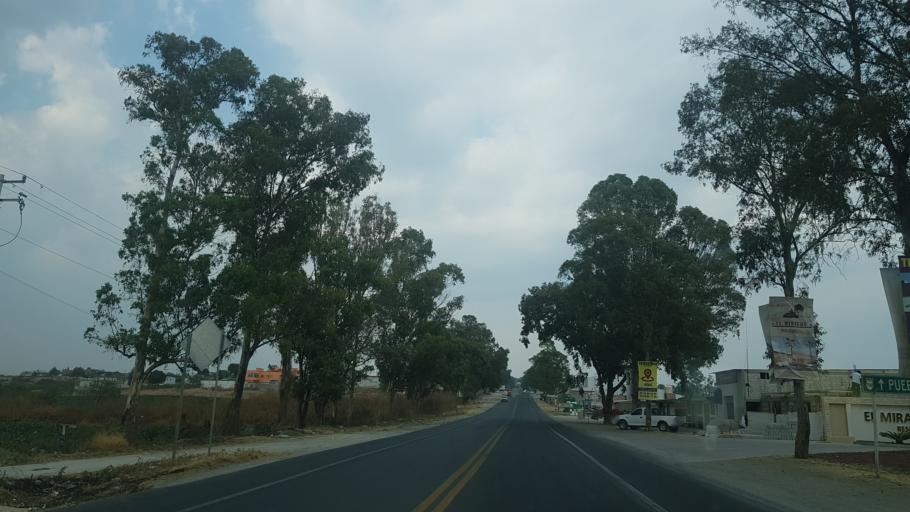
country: MX
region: Puebla
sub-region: Santa Isabel Cholula
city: San Pablo Ahuatempa
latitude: 18.9765
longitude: -98.3727
